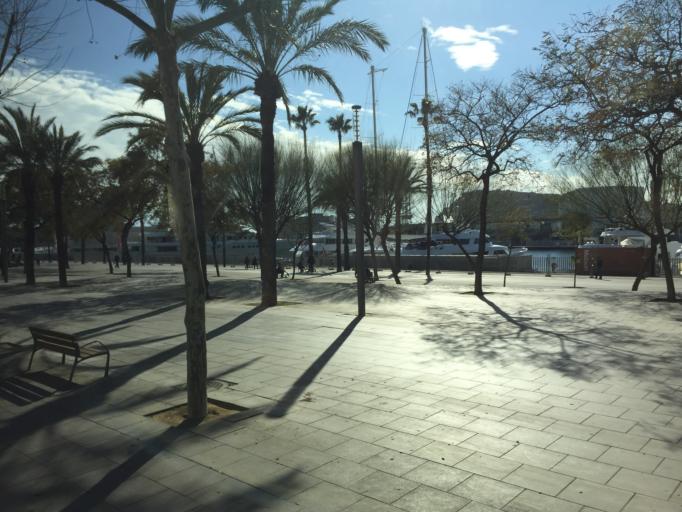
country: ES
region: Catalonia
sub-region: Provincia de Barcelona
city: Ciutat Vella
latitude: 41.3793
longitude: 2.1875
